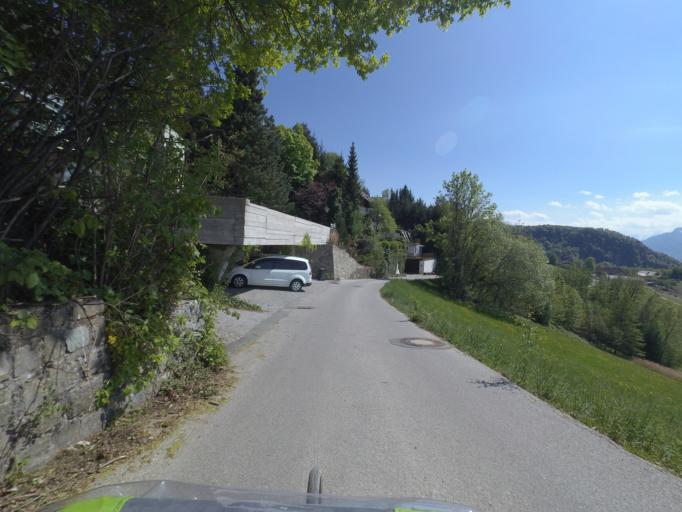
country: AT
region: Salzburg
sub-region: Politischer Bezirk Salzburg-Umgebung
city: Hallwang
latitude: 47.8234
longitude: 13.0856
